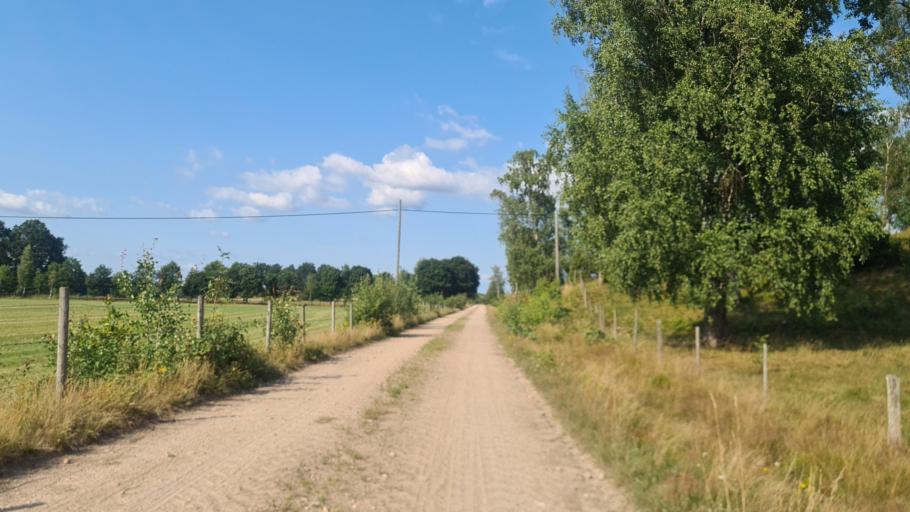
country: SE
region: Kronoberg
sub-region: Ljungby Kommun
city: Ljungby
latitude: 56.7706
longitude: 13.8975
